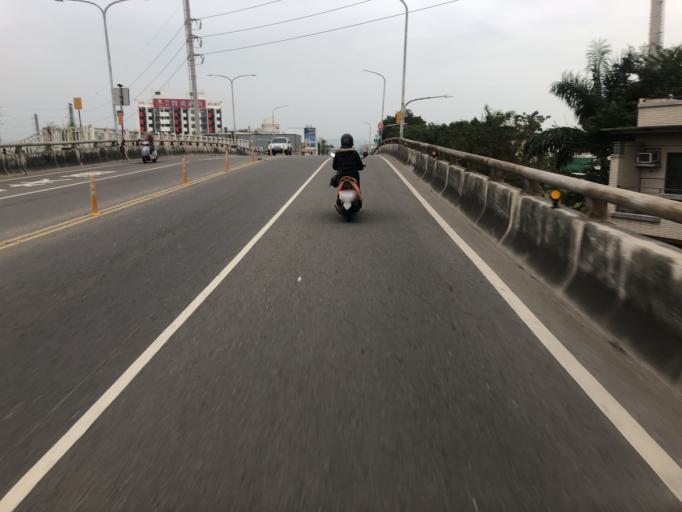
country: TW
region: Taiwan
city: Yujing
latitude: 23.1307
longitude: 120.3054
